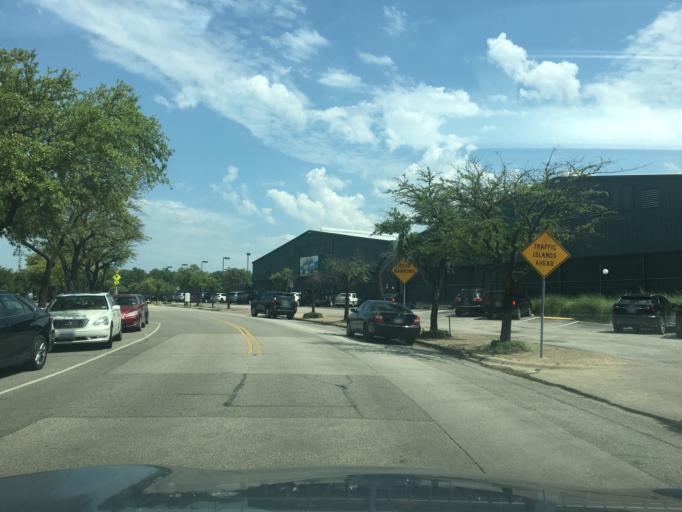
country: US
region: Texas
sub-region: Dallas County
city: Carrollton
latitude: 32.9347
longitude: -96.8595
